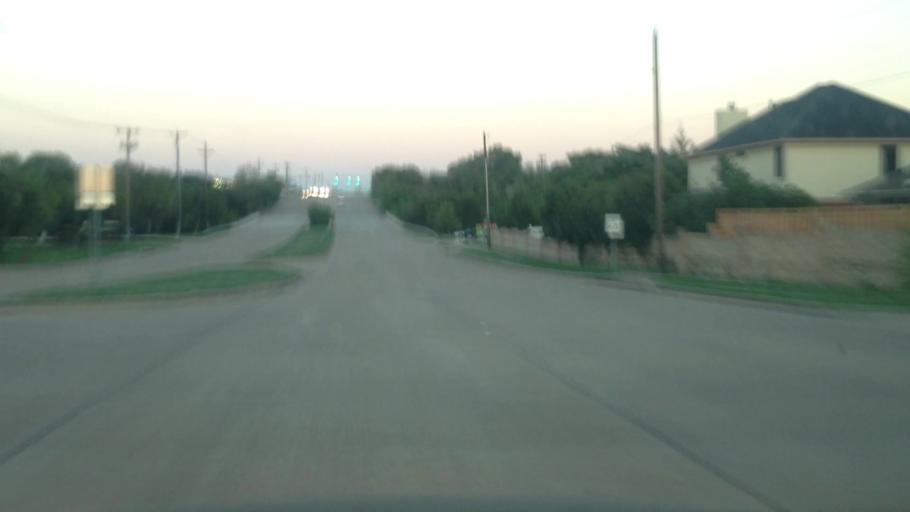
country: US
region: Texas
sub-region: Tarrant County
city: Watauga
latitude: 32.8609
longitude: -97.2712
